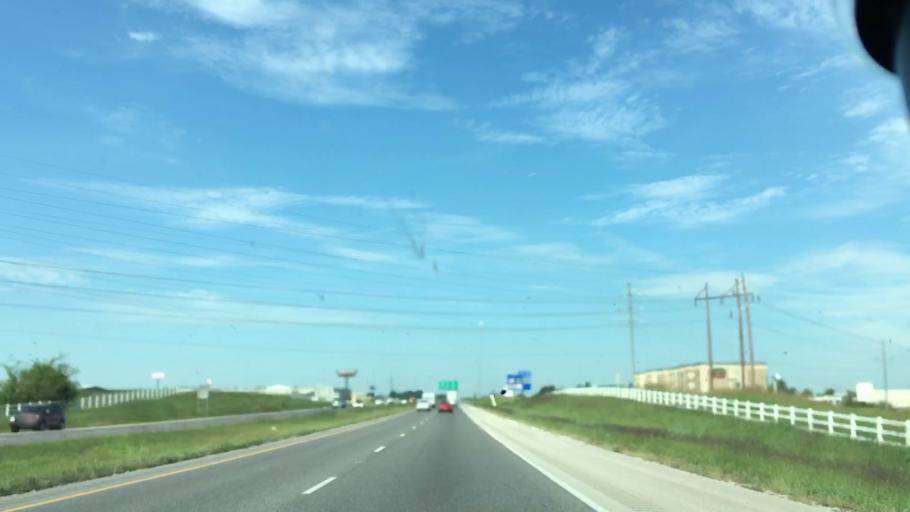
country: US
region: Kentucky
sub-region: Daviess County
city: Owensboro
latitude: 37.7495
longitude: -87.0712
